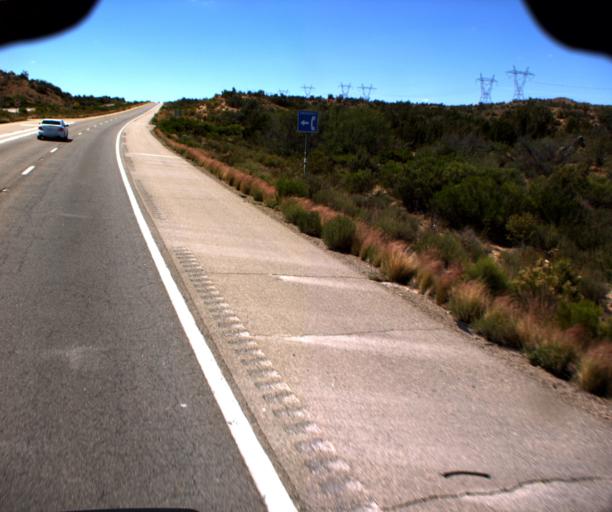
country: US
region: Arizona
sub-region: Yavapai County
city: Bagdad
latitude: 34.4674
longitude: -113.3098
